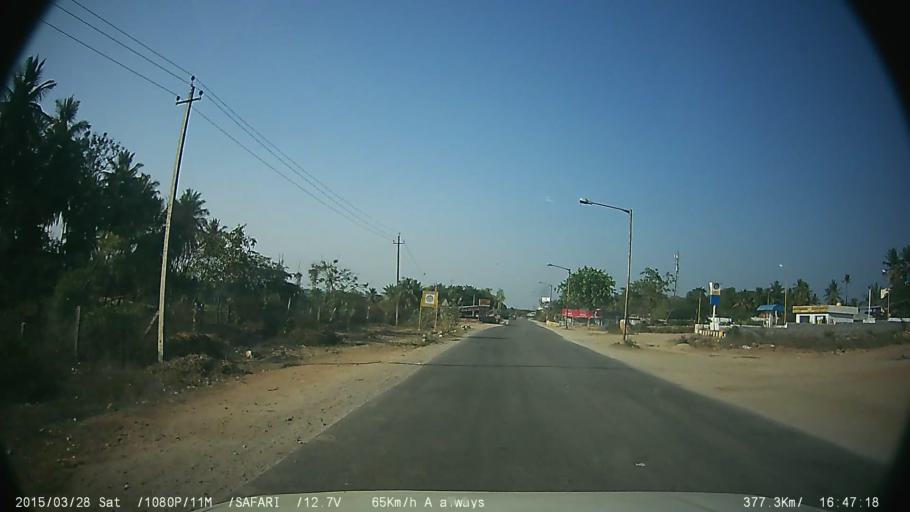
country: IN
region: Karnataka
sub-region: Mandya
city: Shrirangapattana
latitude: 12.4122
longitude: 76.5791
